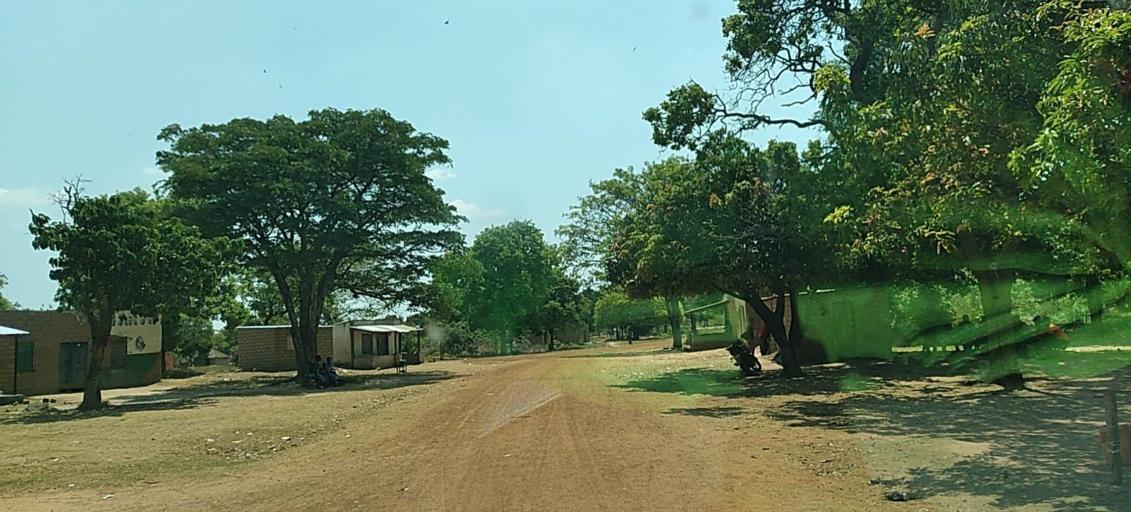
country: CD
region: Katanga
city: Kolwezi
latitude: -11.2975
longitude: 25.2123
